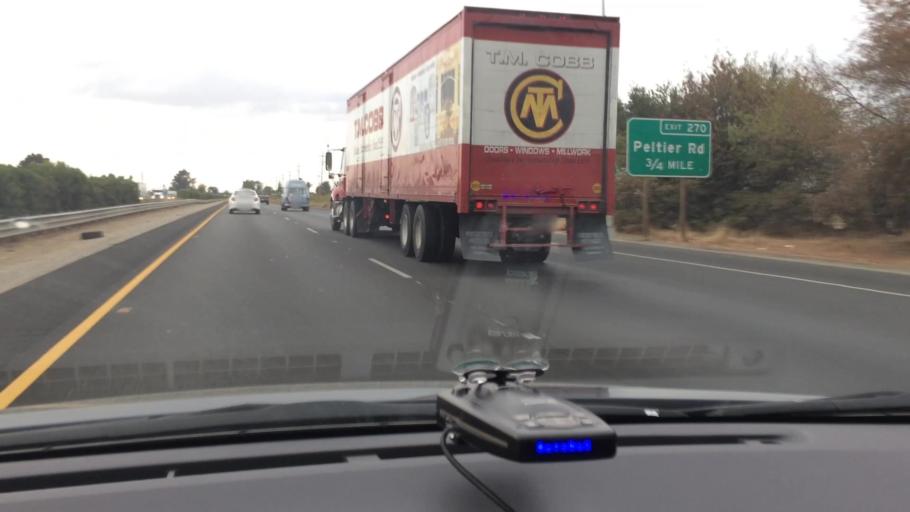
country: US
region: California
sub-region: San Joaquin County
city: Collierville
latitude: 38.1778
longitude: -121.2623
